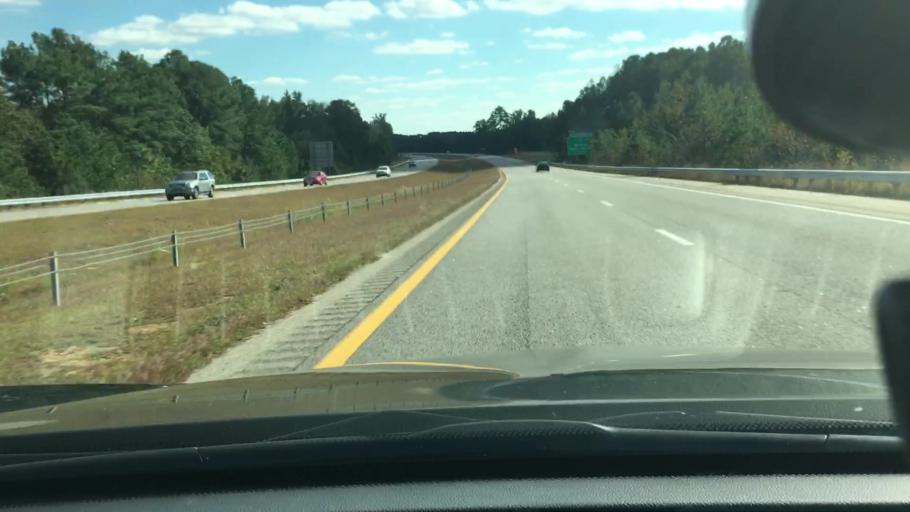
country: US
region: North Carolina
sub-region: Wilson County
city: Lucama
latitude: 35.7473
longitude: -78.0218
